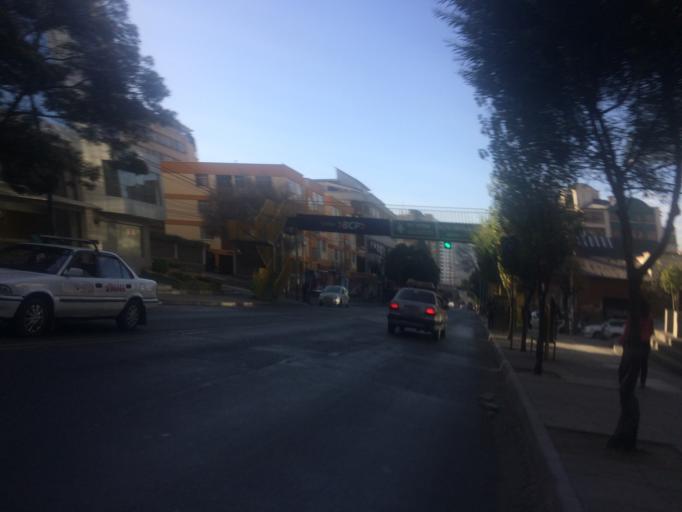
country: BO
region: La Paz
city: La Paz
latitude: -16.5267
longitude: -68.1073
